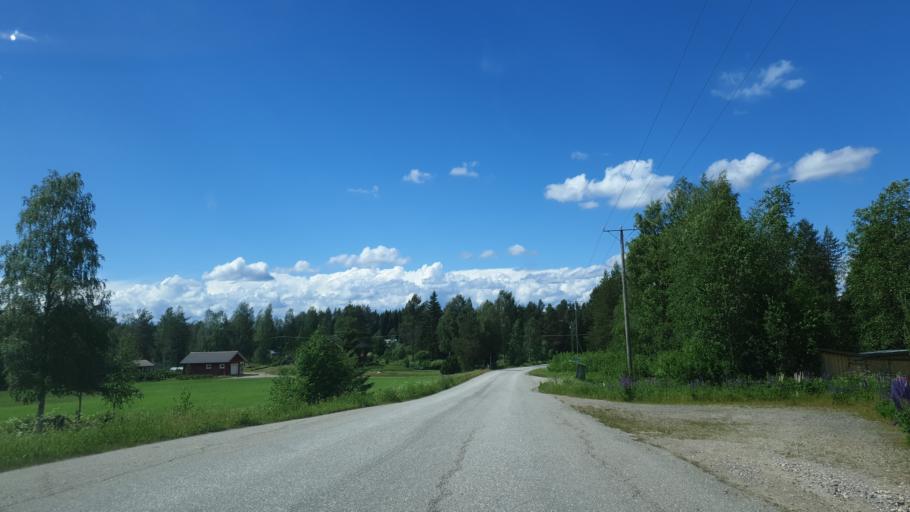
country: FI
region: Northern Savo
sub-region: Koillis-Savo
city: Kaavi
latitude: 63.0019
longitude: 28.6836
